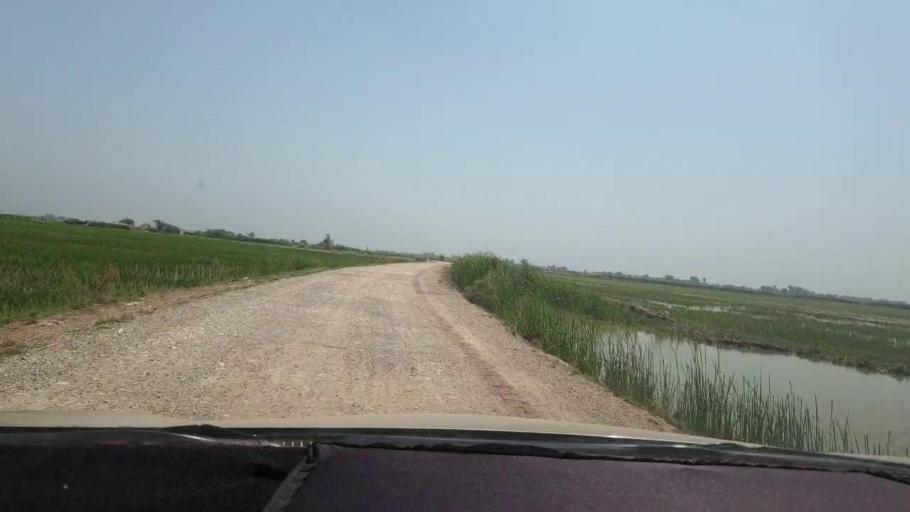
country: PK
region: Sindh
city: Shahdadkot
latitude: 27.8262
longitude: 67.9901
